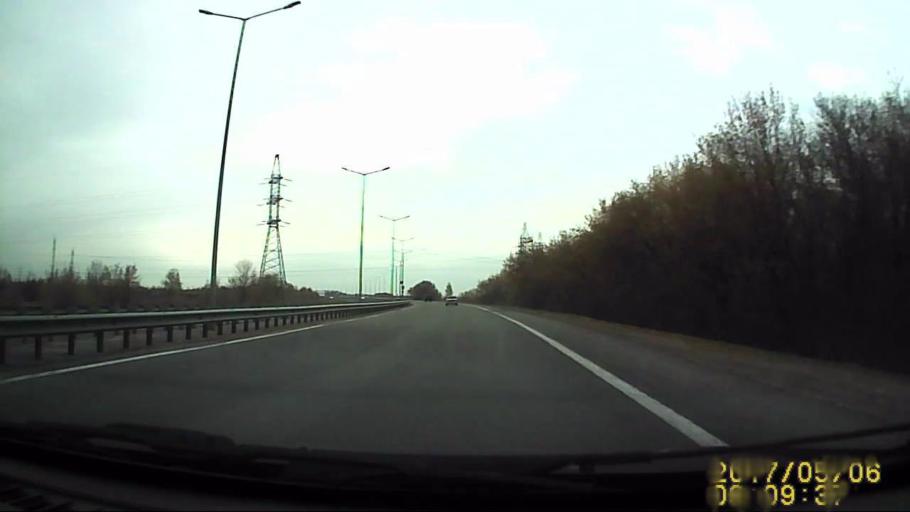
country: RU
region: Ulyanovsk
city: Mirnyy
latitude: 54.3438
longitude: 48.6409
